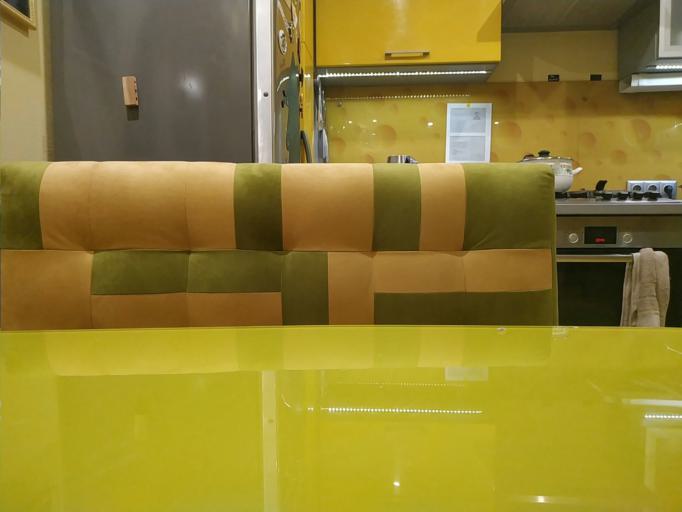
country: RU
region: Murmansk
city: Alakurtti
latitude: 66.2815
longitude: 30.2529
